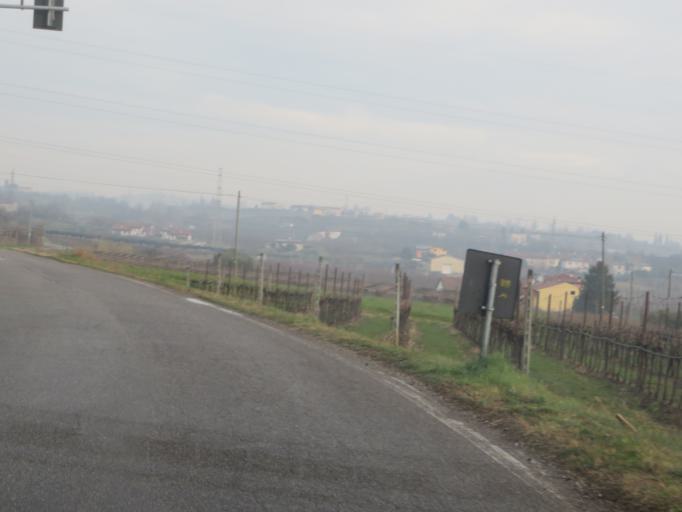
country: IT
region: Veneto
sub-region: Provincia di Verona
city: Sandra
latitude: 45.4587
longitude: 10.8195
